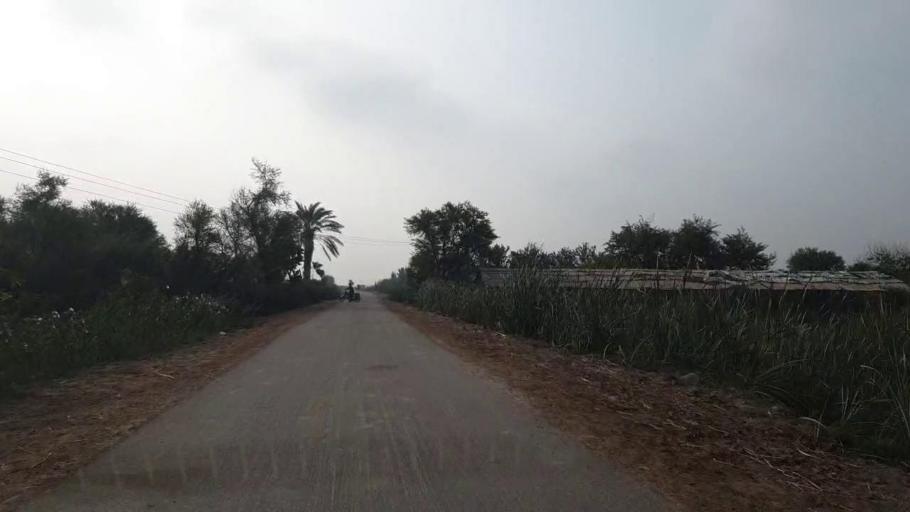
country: PK
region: Sindh
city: Tando Muhammad Khan
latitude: 25.1336
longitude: 68.5947
